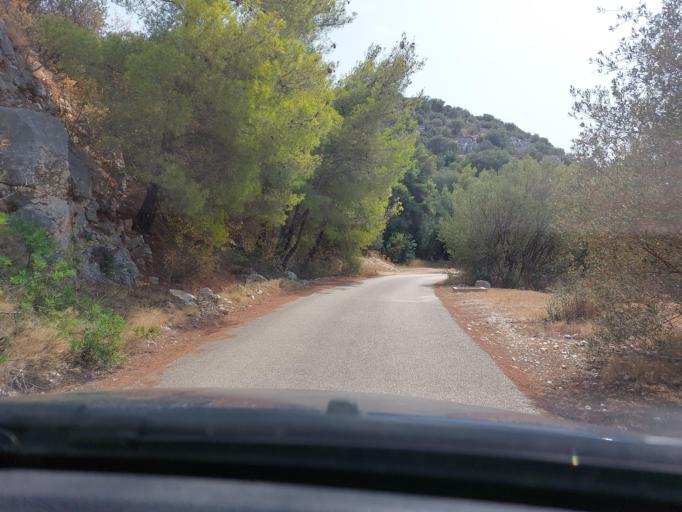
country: HR
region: Dubrovacko-Neretvanska
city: Smokvica
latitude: 42.7317
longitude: 16.8927
